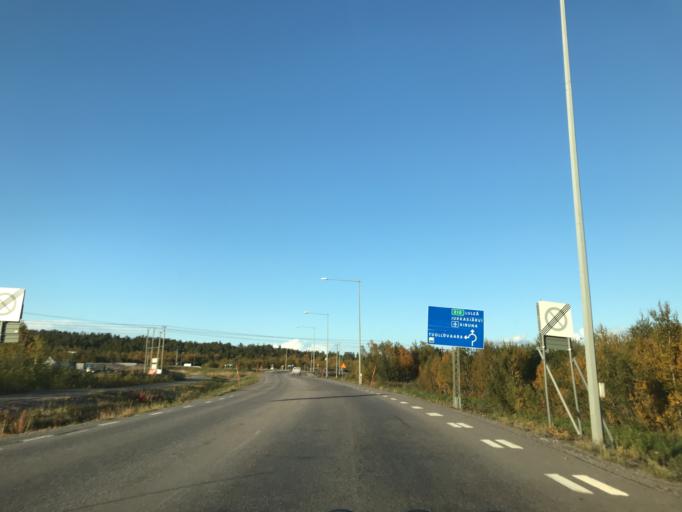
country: SE
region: Norrbotten
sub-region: Kiruna Kommun
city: Kiruna
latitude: 67.8449
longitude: 20.3143
